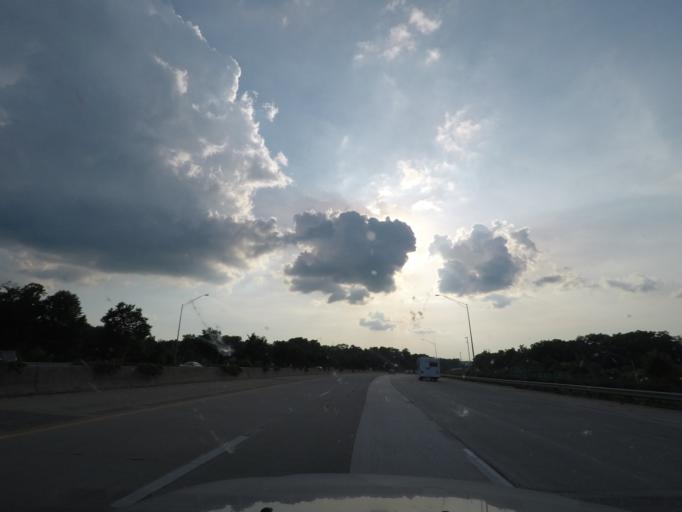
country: US
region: North Carolina
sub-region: Durham County
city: Durham
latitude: 36.0145
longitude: -78.8885
